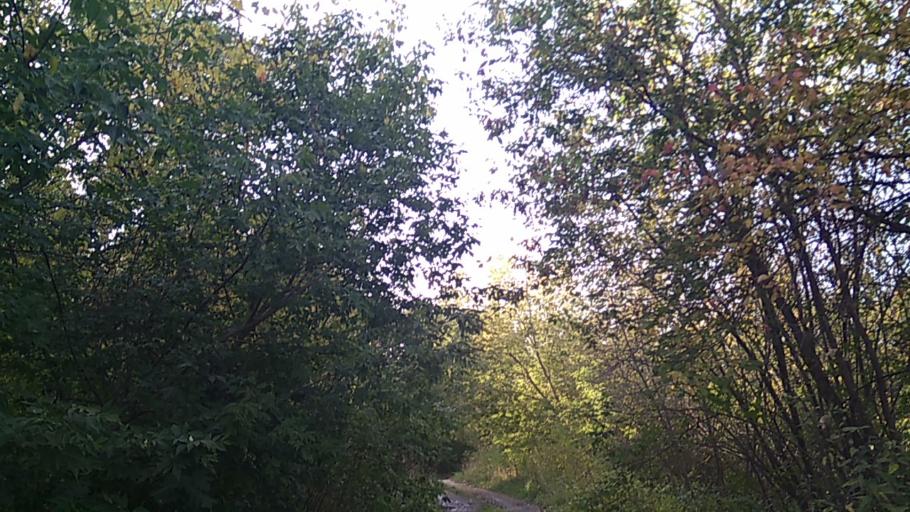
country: RU
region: Sverdlovsk
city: Pokrovskoye
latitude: 56.4339
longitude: 61.5945
